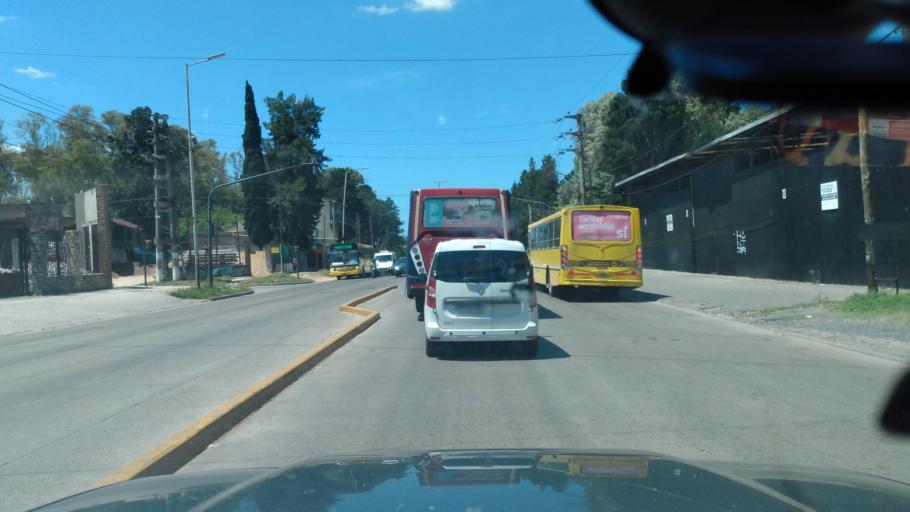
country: AR
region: Buenos Aires
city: Hurlingham
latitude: -34.5606
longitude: -58.7325
